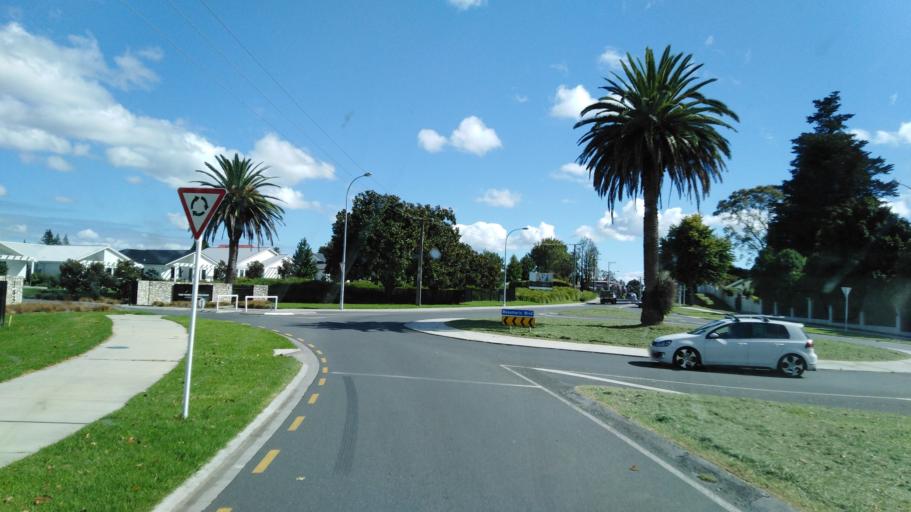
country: NZ
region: Bay of Plenty
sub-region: Tauranga City
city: Tauranga
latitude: -37.7012
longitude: 176.1135
